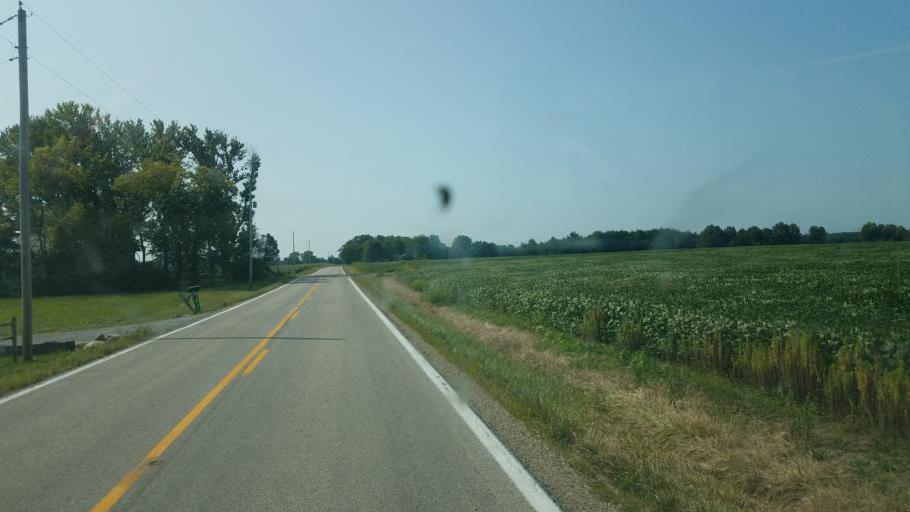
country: US
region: Ohio
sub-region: Delaware County
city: Ashley
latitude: 40.4811
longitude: -82.9638
